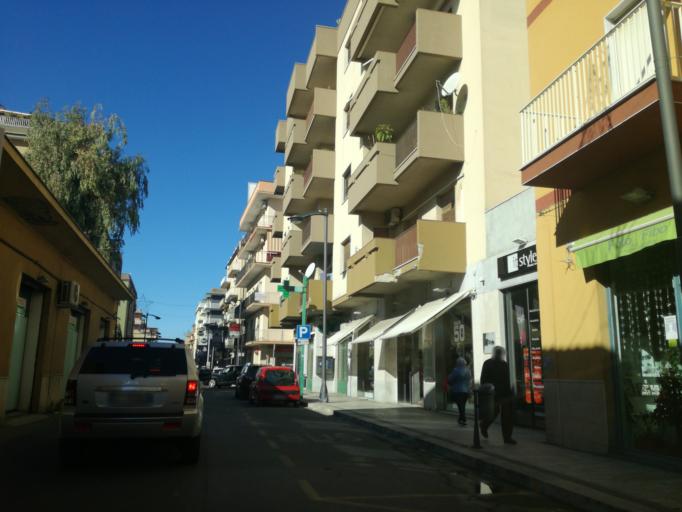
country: IT
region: Sicily
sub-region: Provincia di Caltanissetta
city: Gela
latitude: 37.0730
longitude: 14.2342
